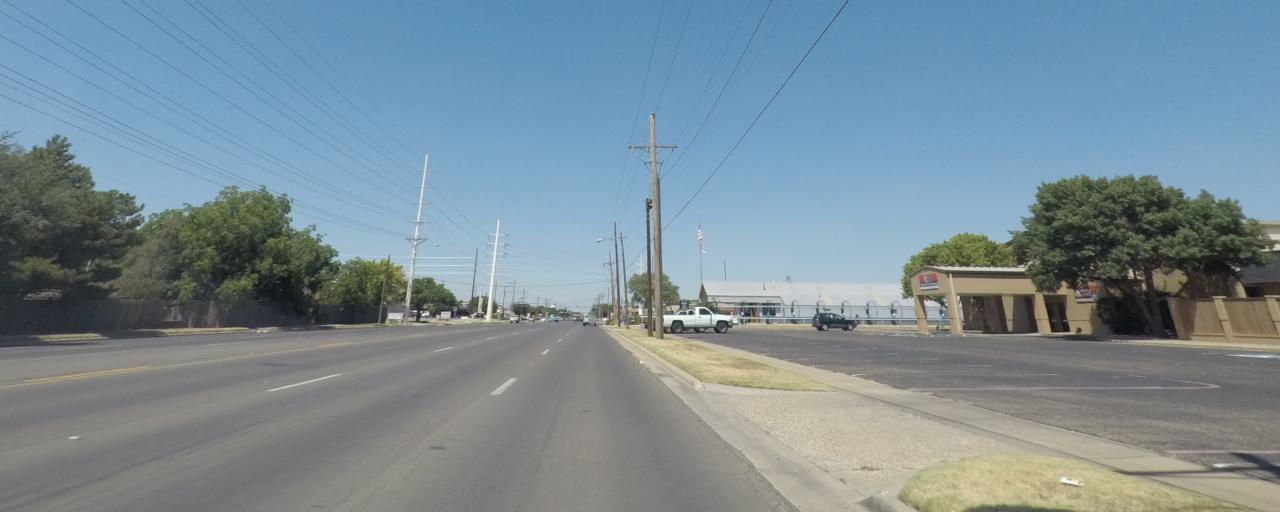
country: US
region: Texas
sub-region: Lubbock County
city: Lubbock
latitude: 33.5172
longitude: -101.8876
